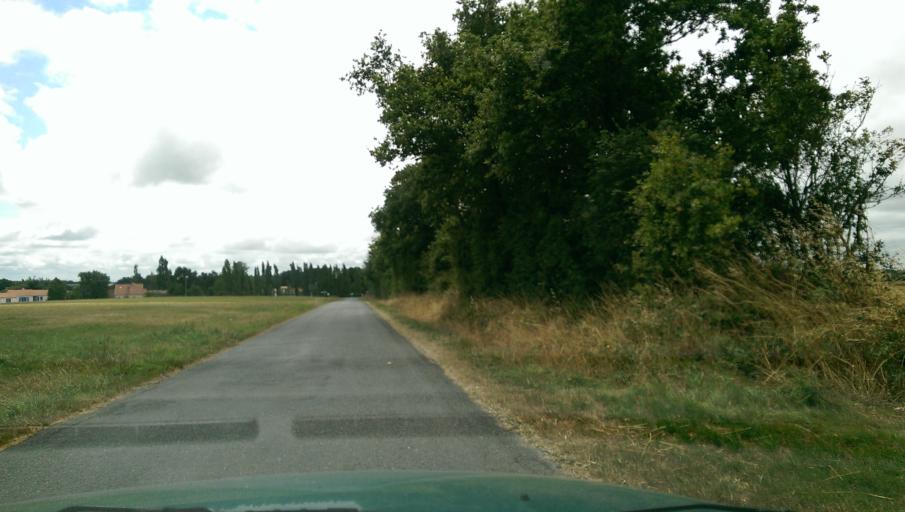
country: FR
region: Pays de la Loire
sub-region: Departement de la Loire-Atlantique
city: Remouille
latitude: 47.0608
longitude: -1.3633
